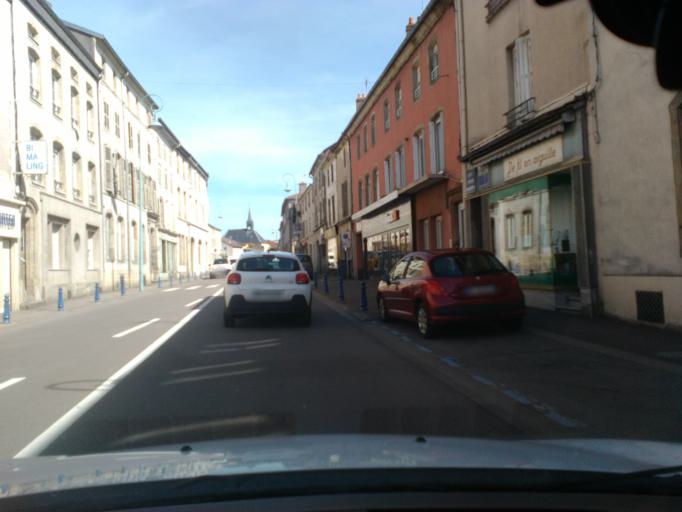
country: FR
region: Lorraine
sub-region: Departement des Vosges
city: Mirecourt
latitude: 48.3039
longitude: 6.1344
